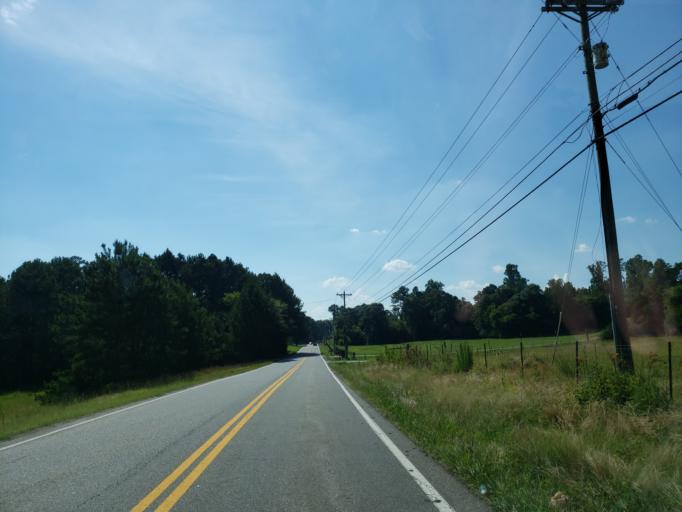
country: US
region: Georgia
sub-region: Cherokee County
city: Woodstock
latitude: 34.1157
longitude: -84.4606
